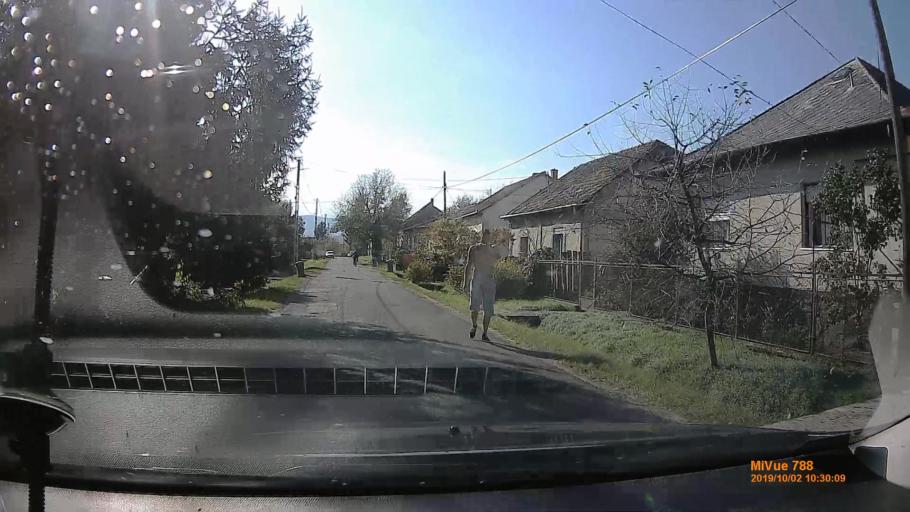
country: HU
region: Nograd
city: Kazar
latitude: 48.0186
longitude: 19.8261
